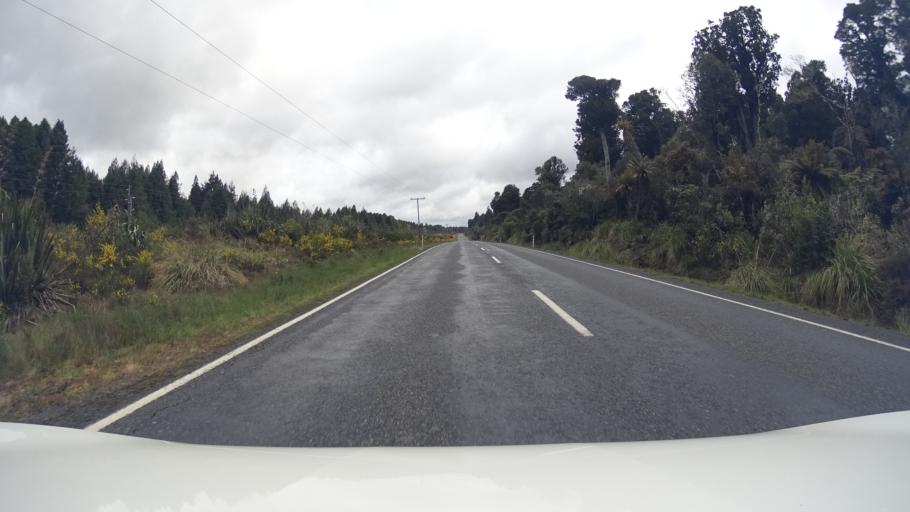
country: NZ
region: Manawatu-Wanganui
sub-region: Ruapehu District
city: Waiouru
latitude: -39.2546
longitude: 175.3878
